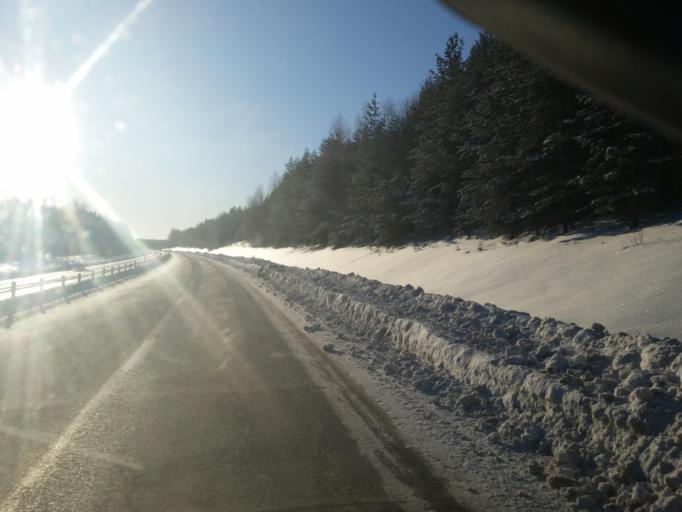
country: SE
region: Norrbotten
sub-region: Pitea Kommun
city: Bergsviken
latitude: 65.3061
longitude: 21.4089
